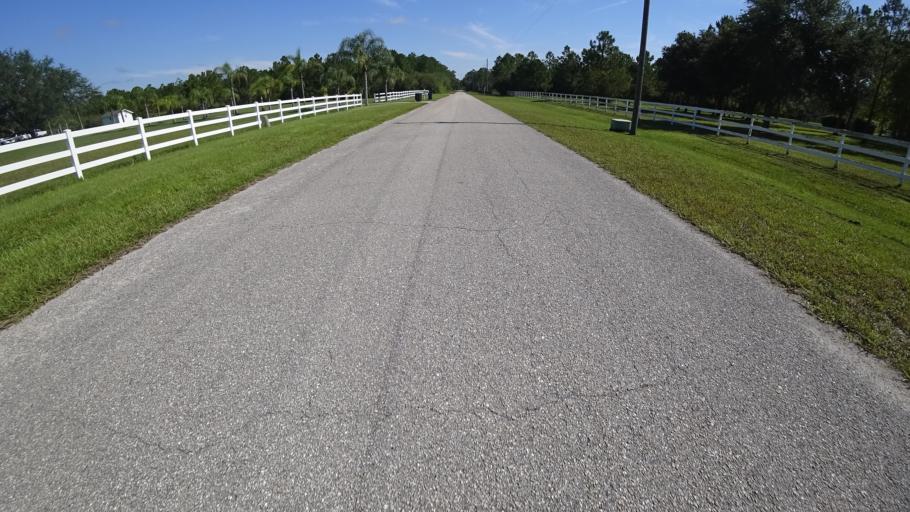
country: US
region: Florida
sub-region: Sarasota County
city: The Meadows
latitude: 27.4229
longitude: -82.3285
